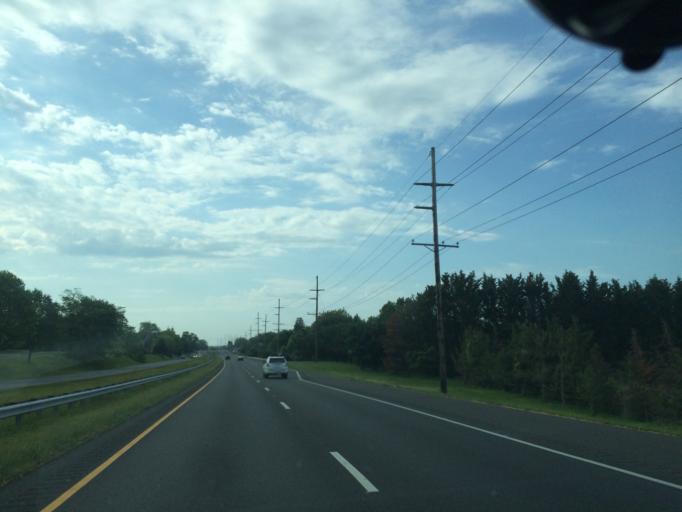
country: US
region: Maryland
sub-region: Baltimore County
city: Reisterstown
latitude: 39.5059
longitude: -76.9022
